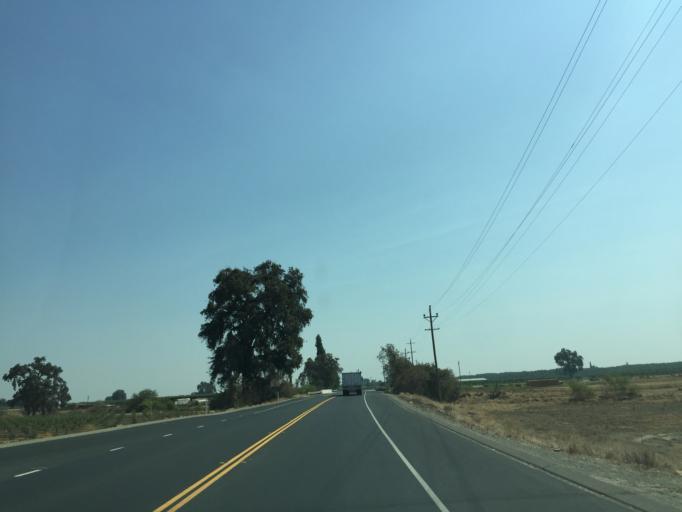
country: US
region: California
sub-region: Fresno County
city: Laton
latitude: 36.4309
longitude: -119.6363
